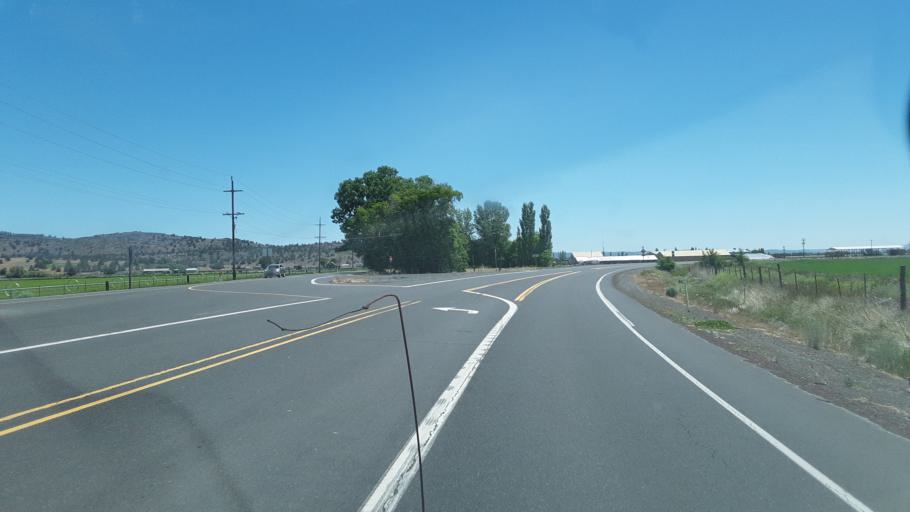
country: US
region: California
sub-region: Siskiyou County
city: Tulelake
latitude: 42.0240
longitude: -121.5507
